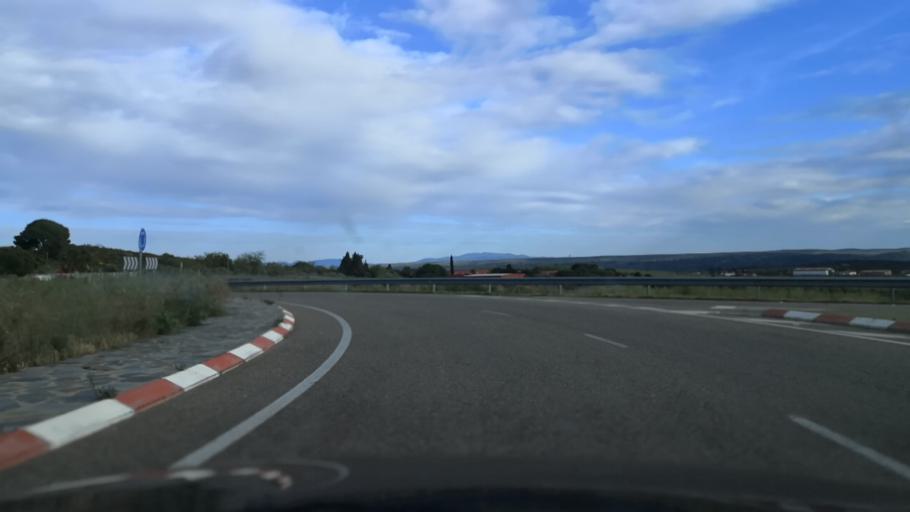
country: ES
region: Extremadura
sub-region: Provincia de Caceres
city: Coria
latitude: 40.0089
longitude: -6.5612
